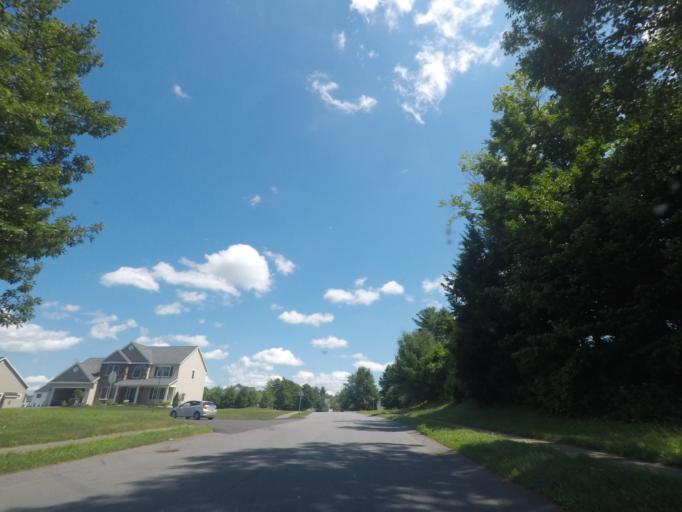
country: US
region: New York
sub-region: Schenectady County
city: Rotterdam
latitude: 42.7443
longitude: -73.9404
